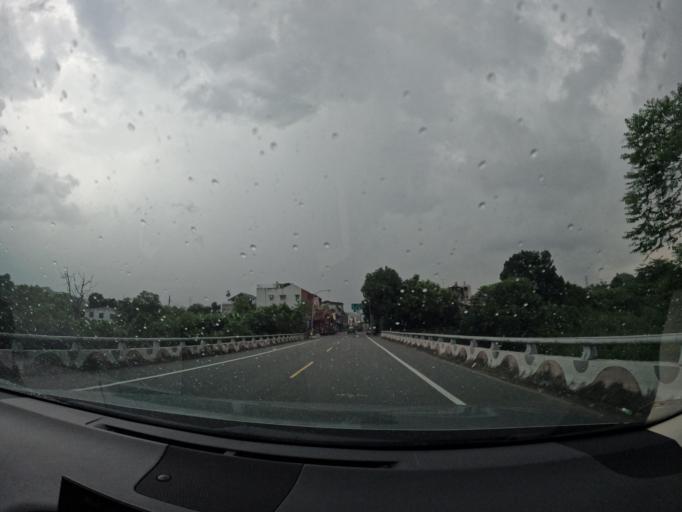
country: TW
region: Taiwan
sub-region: Nantou
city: Nantou
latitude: 23.8785
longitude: 120.7696
